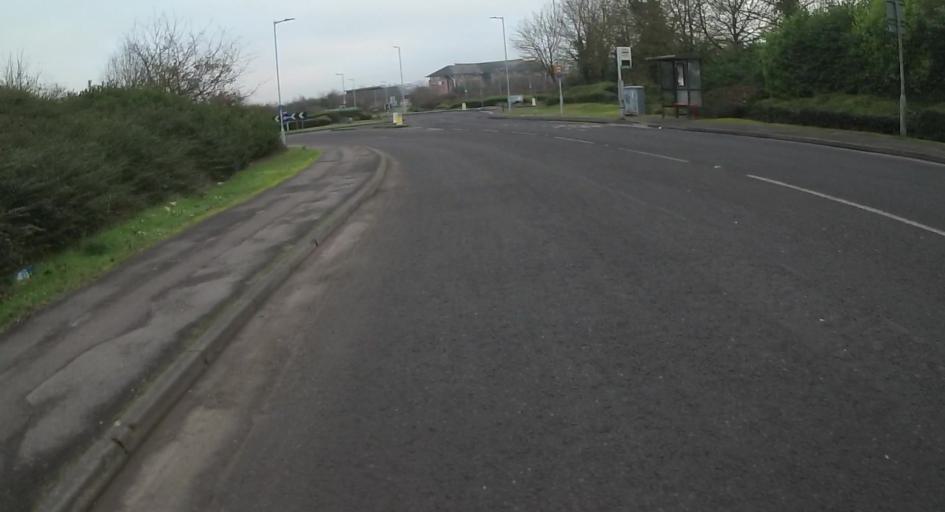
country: GB
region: England
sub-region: Bracknell Forest
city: Binfield
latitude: 51.4155
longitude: -0.7833
